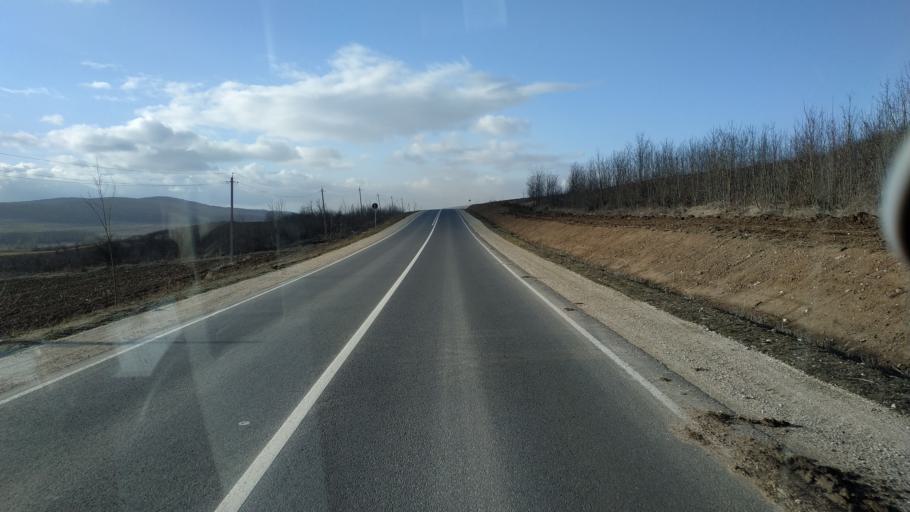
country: MD
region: Calarasi
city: Calarasi
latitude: 47.3092
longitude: 28.1265
